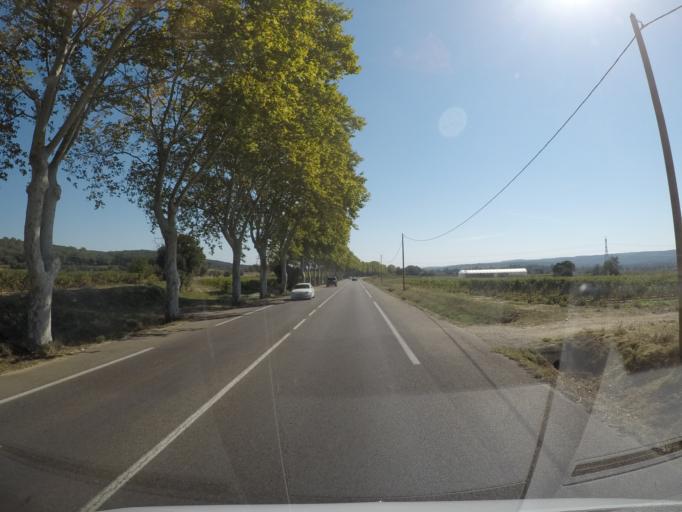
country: FR
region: Languedoc-Roussillon
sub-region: Departement du Gard
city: Uzes
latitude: 43.9855
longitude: 4.4574
